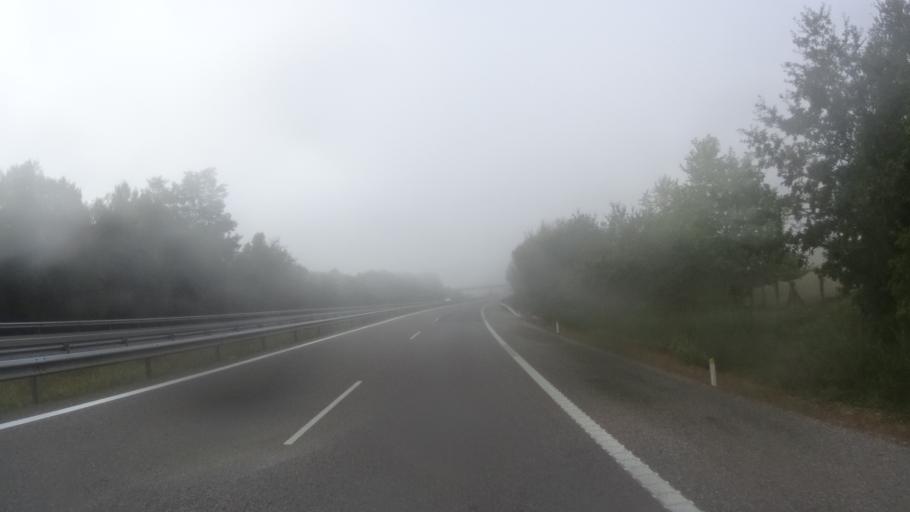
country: ES
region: Galicia
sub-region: Provincia da Coruna
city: Oroso
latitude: 43.0020
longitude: -8.4210
